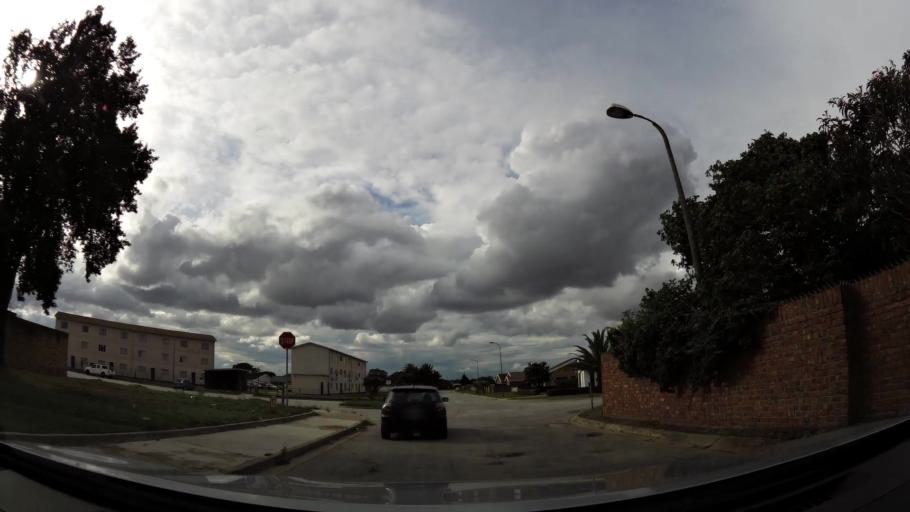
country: ZA
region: Eastern Cape
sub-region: Nelson Mandela Bay Metropolitan Municipality
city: Port Elizabeth
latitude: -33.9404
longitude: 25.5025
